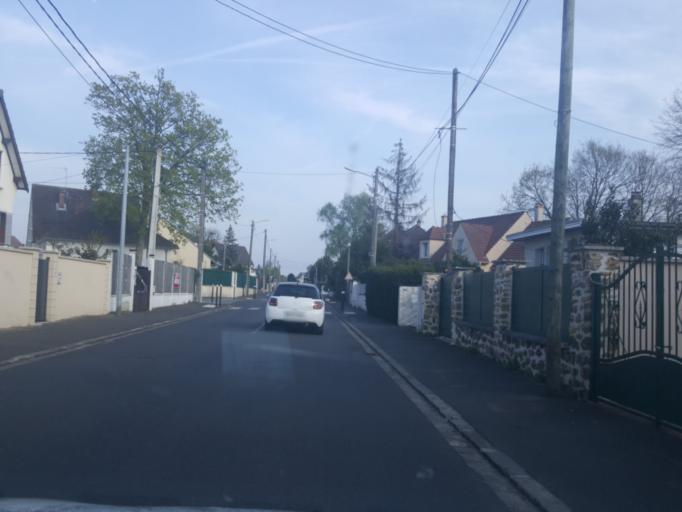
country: FR
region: Ile-de-France
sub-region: Departement de l'Essonne
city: Sainte-Genevieve-des-Bois
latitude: 48.6438
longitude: 2.3151
